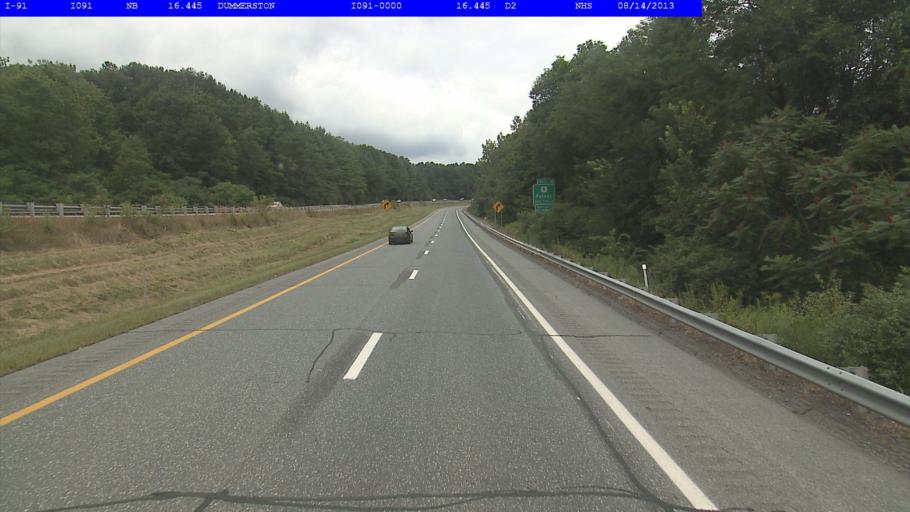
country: US
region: New Hampshire
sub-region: Cheshire County
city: Chesterfield
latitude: 42.9459
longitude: -72.5320
